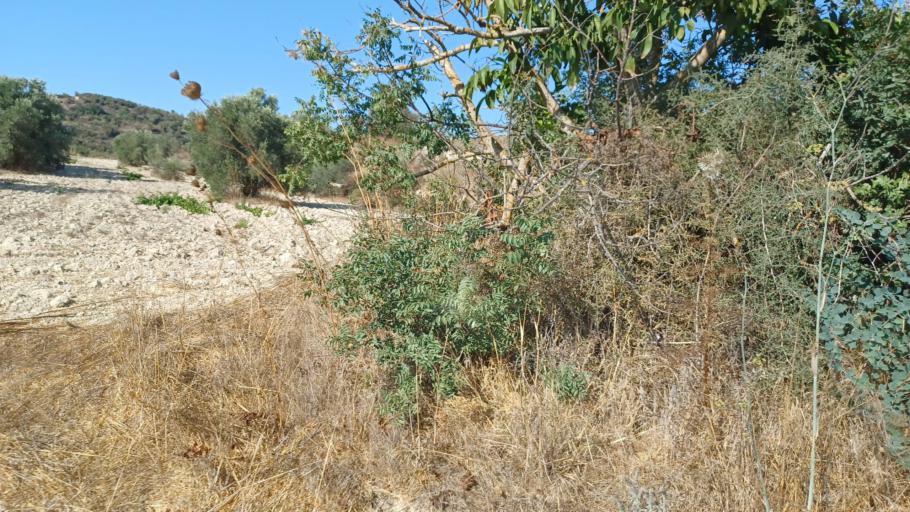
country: CY
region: Pafos
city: Mesogi
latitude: 34.8752
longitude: 32.5312
